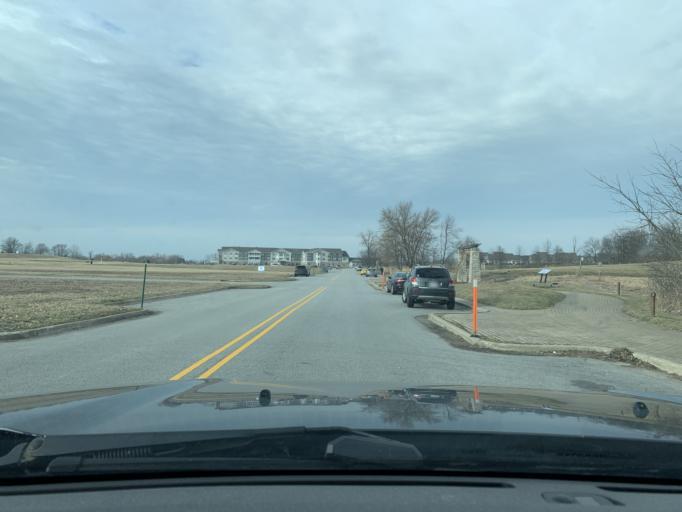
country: US
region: Indiana
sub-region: Porter County
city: Chesterton
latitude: 41.5820
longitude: -87.0421
